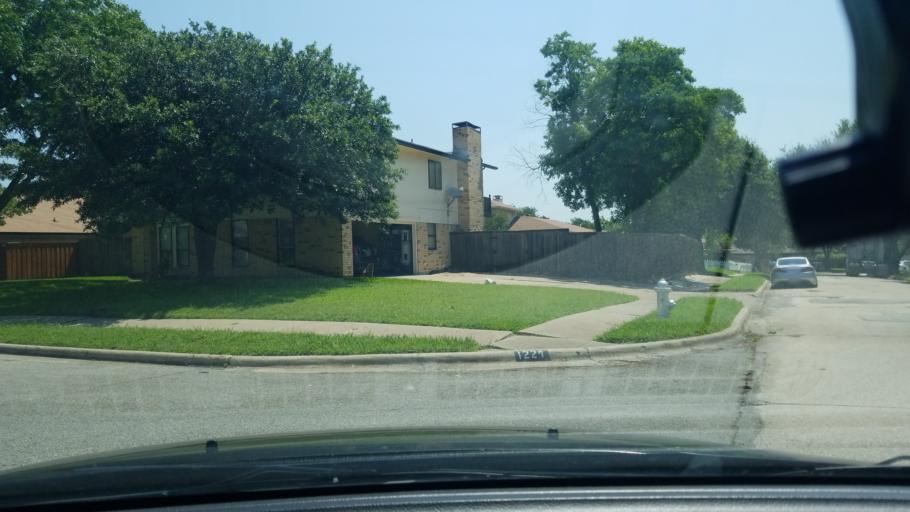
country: US
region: Texas
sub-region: Dallas County
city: Sunnyvale
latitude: 32.8276
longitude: -96.6130
